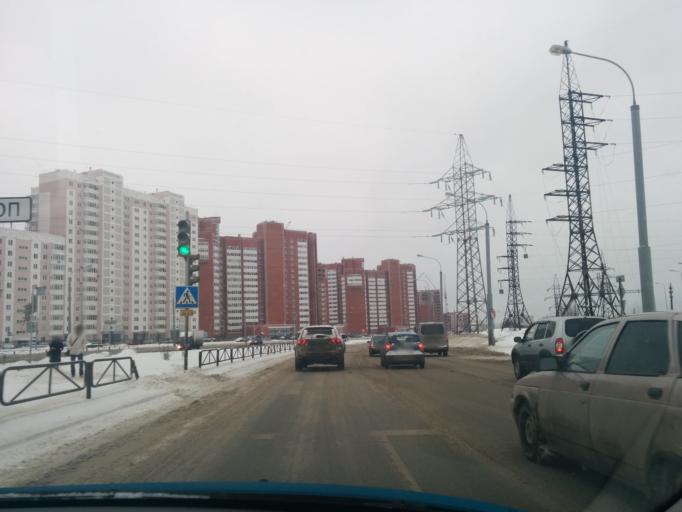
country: RU
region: Perm
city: Perm
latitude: 57.9879
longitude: 56.2927
